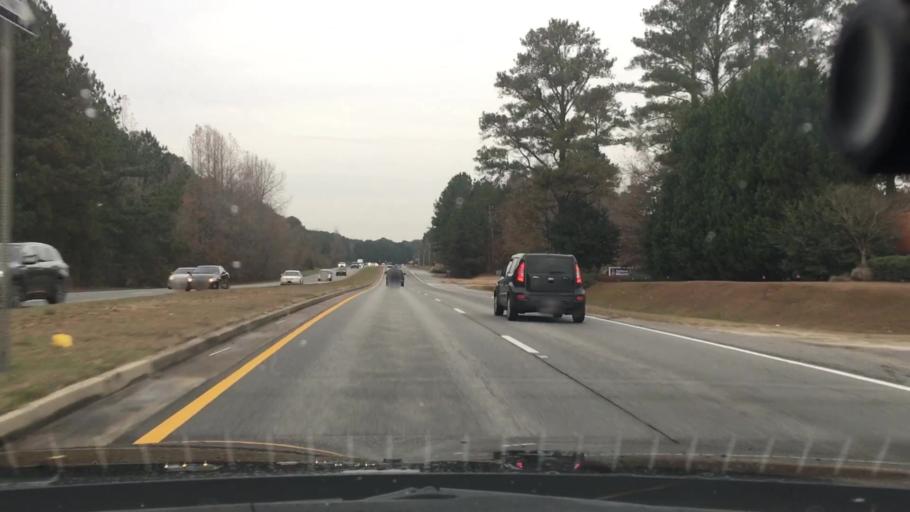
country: US
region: Georgia
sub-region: Fayette County
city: Peachtree City
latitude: 33.4148
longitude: -84.6027
